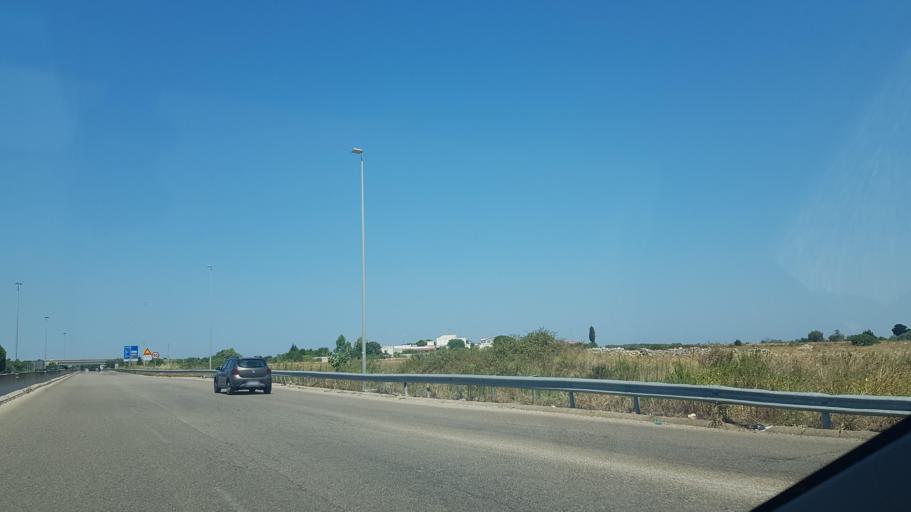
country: IT
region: Apulia
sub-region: Provincia di Lecce
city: Merine
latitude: 40.3470
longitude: 18.2058
